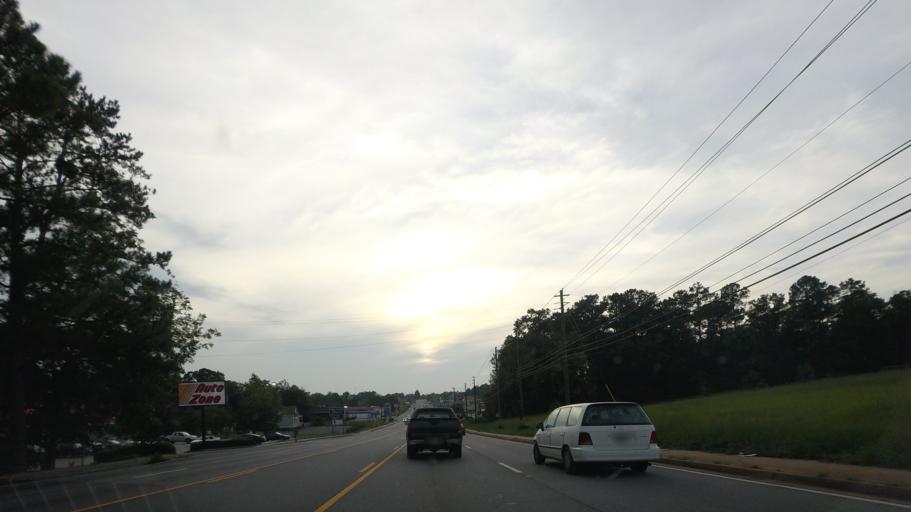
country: US
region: Georgia
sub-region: Bibb County
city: Macon
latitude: 32.8596
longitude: -83.6082
